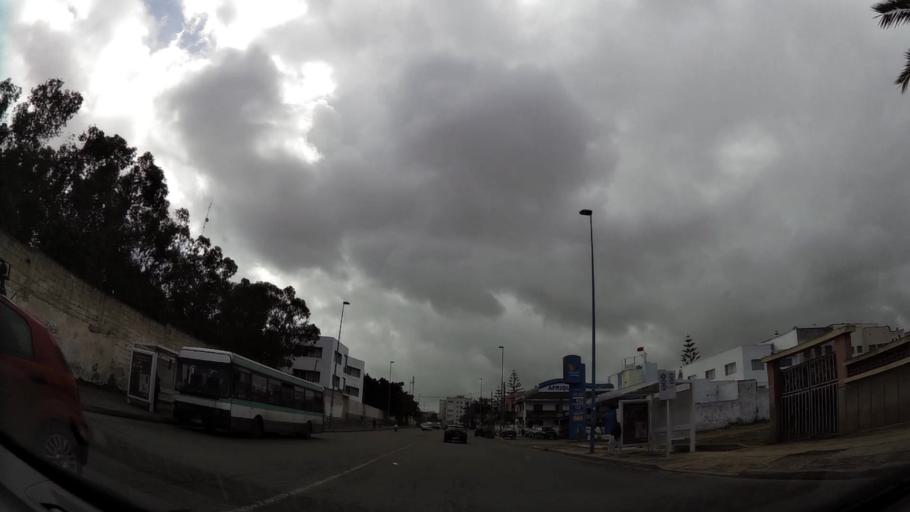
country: MA
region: Grand Casablanca
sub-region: Casablanca
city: Casablanca
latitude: 33.5422
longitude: -7.6012
